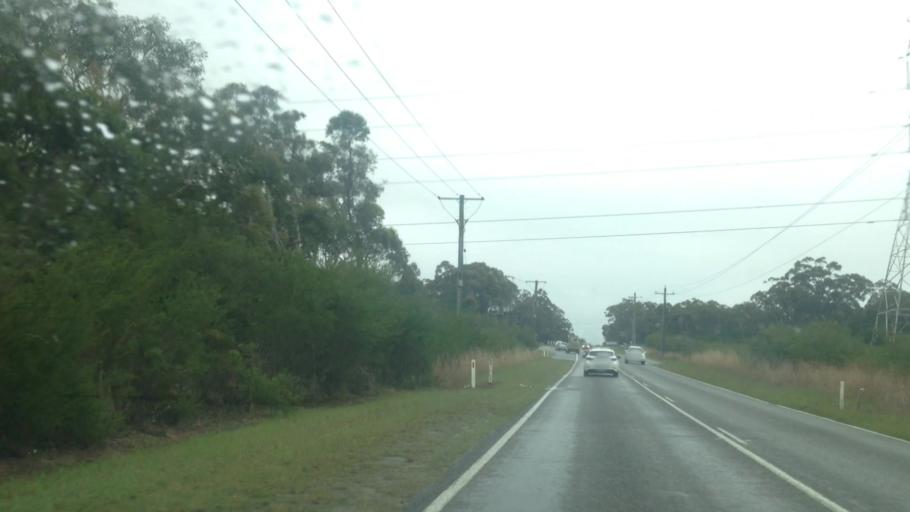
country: AU
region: New South Wales
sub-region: Wyong Shire
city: Charmhaven
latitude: -33.1587
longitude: 151.4786
